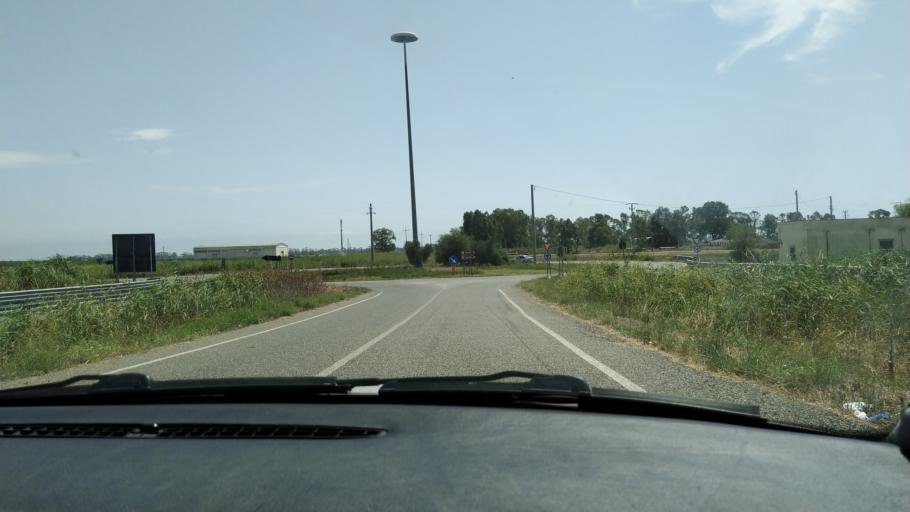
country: IT
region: Basilicate
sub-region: Provincia di Matera
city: Marconia
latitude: 40.3404
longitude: 16.7625
